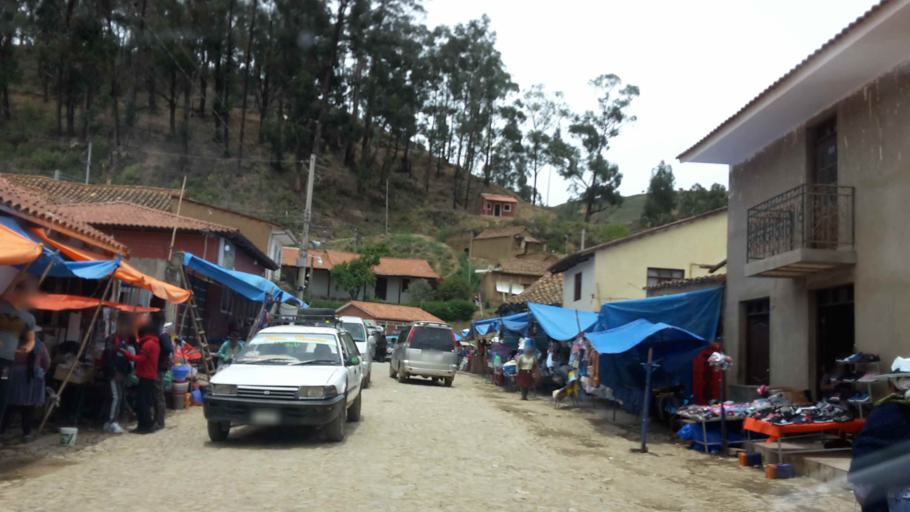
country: BO
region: Cochabamba
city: Totora
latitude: -17.7349
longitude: -65.1917
